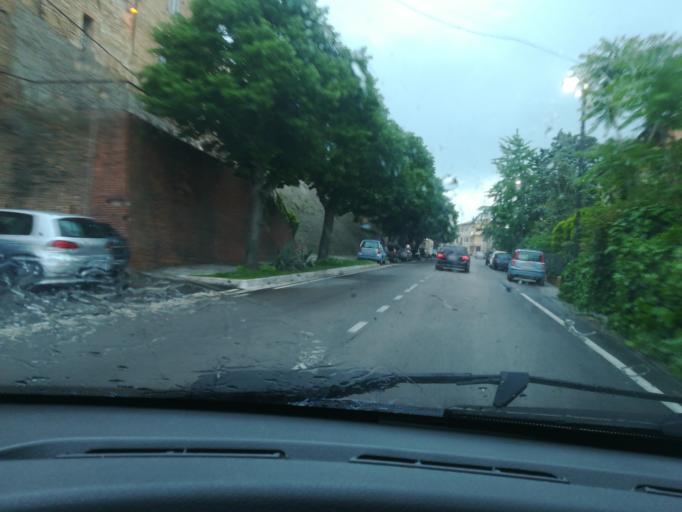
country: IT
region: The Marches
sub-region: Provincia di Macerata
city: Treia
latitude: 43.3123
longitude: 13.3106
